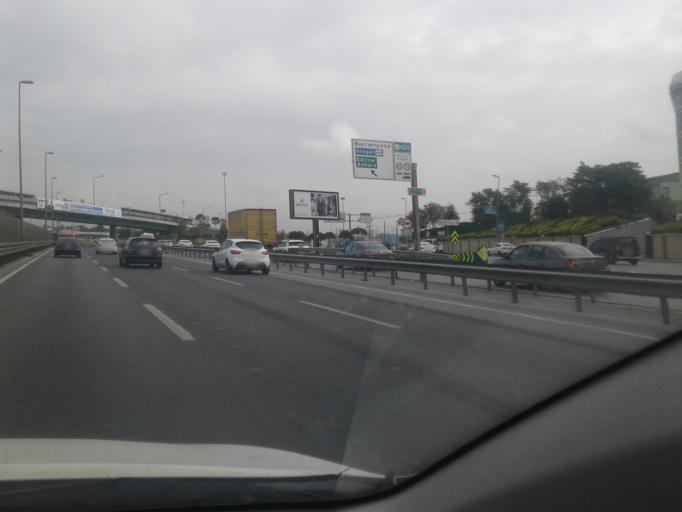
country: TR
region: Istanbul
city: Zeytinburnu
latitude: 41.0176
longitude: 28.9131
